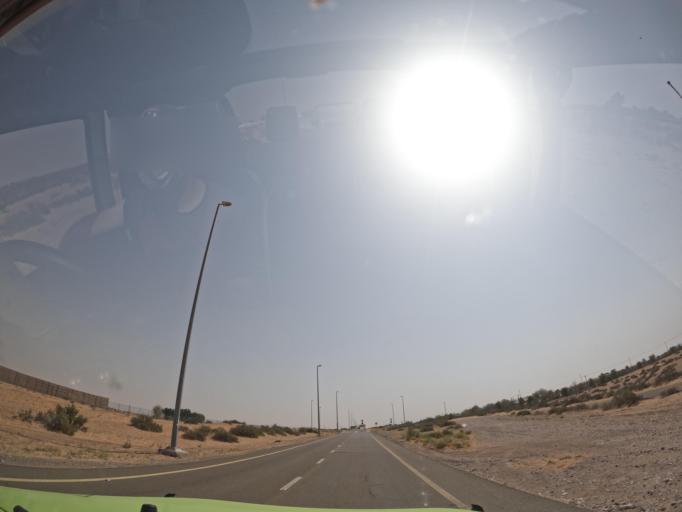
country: OM
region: Al Buraimi
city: Al Buraymi
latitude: 24.6885
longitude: 55.5973
